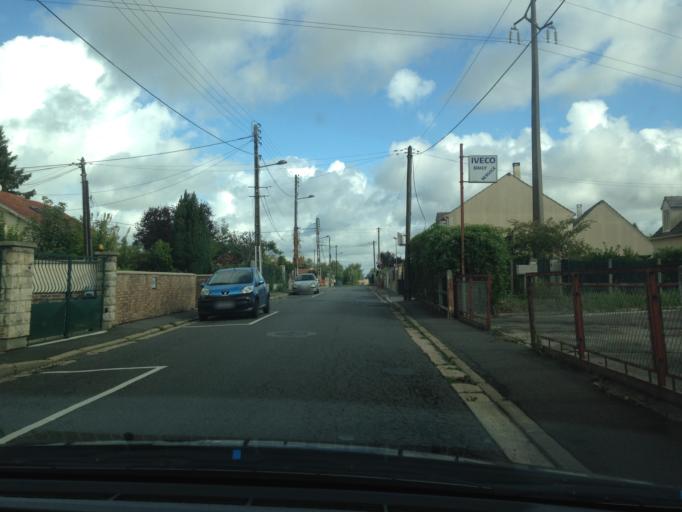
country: FR
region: Ile-de-France
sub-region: Departement du Val-d'Oise
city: Osny
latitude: 49.0709
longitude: 2.0694
